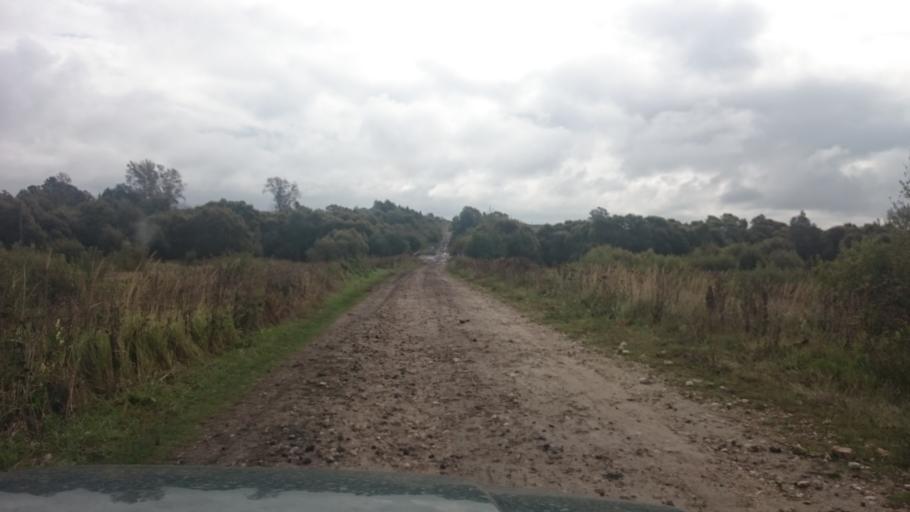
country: RU
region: Mordoviya
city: Kadoshkino
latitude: 54.0190
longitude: 44.4531
